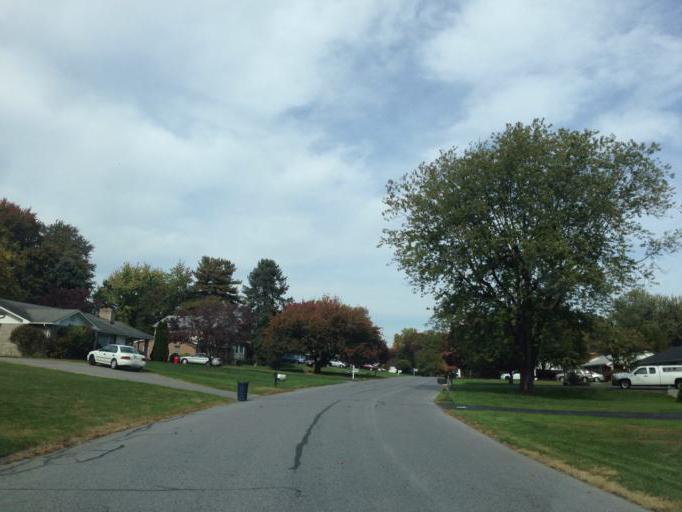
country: US
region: Maryland
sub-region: Howard County
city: Columbia
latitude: 39.2914
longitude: -76.8519
